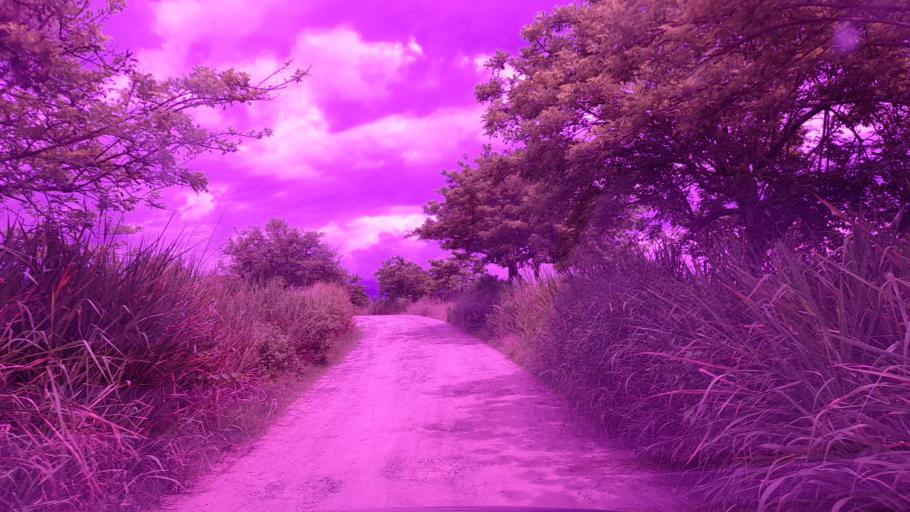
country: CO
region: Valle del Cauca
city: Bugalagrande
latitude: 4.1943
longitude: -76.1428
